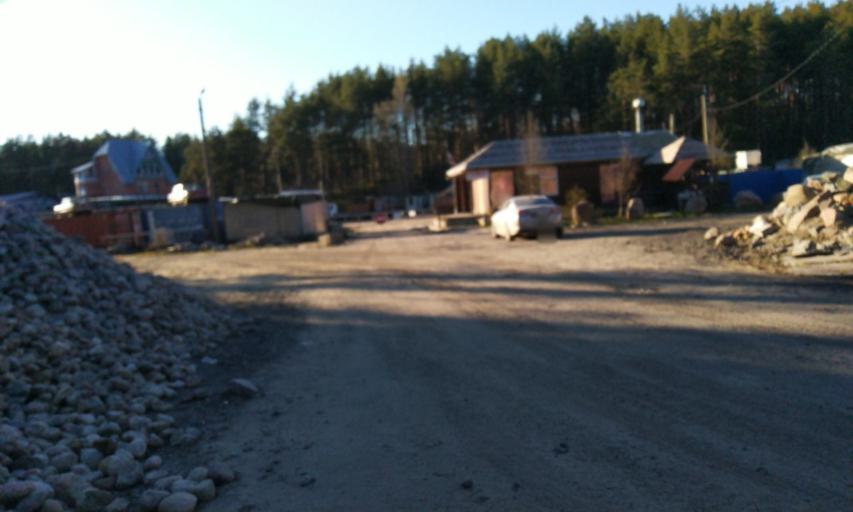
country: RU
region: Leningrad
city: Toksovo
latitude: 60.1290
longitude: 30.5193
